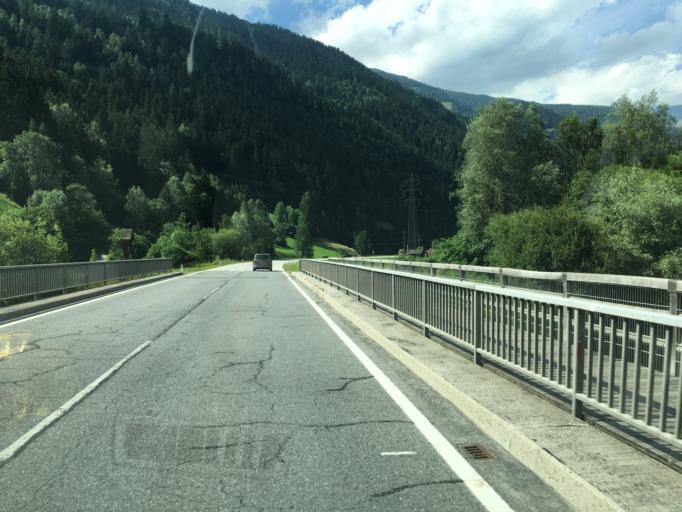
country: AT
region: Carinthia
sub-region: Politischer Bezirk Spittal an der Drau
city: Stall
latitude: 46.9051
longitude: 13.0678
